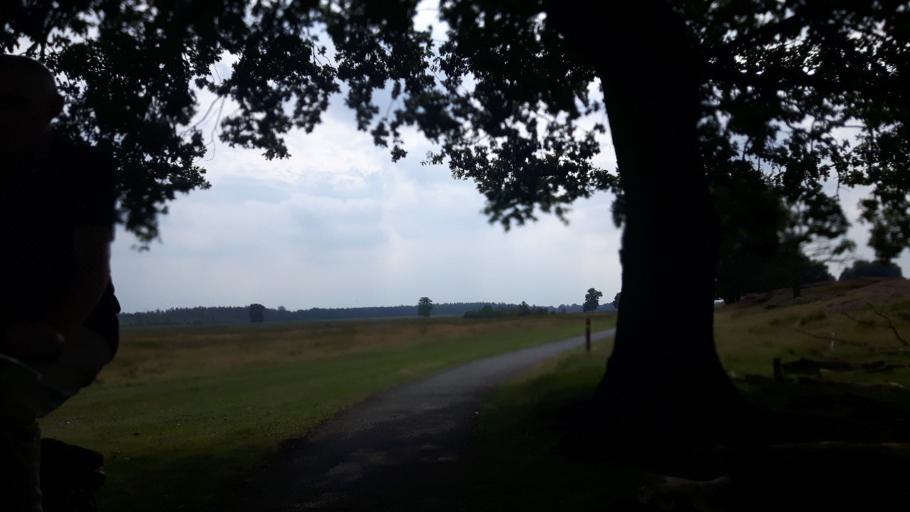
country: NL
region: Drenthe
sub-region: Gemeente Westerveld
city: Dwingeloo
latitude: 52.9291
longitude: 6.3075
